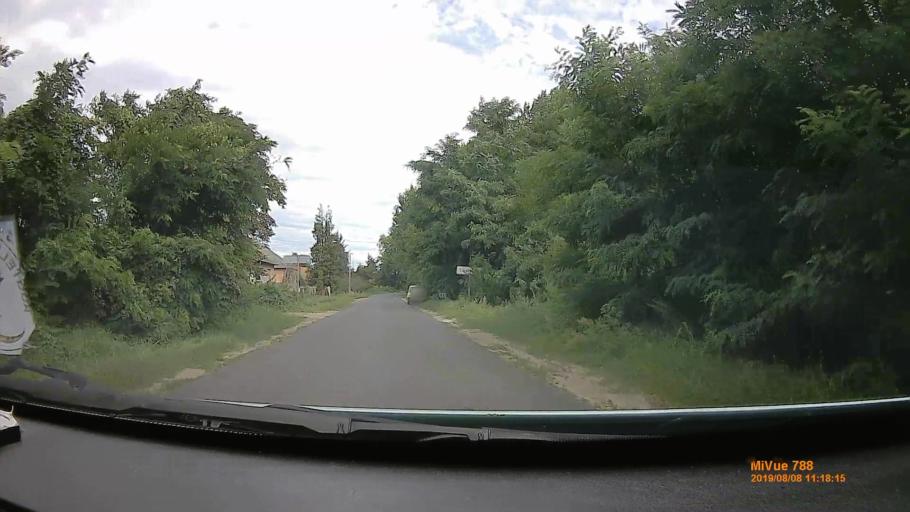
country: HU
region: Szabolcs-Szatmar-Bereg
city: Balkany
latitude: 47.7362
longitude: 21.8363
